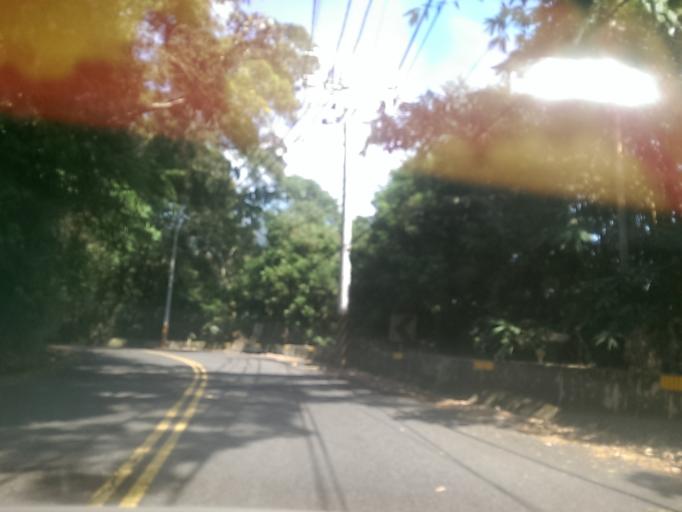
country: TW
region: Taiwan
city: Lugu
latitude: 23.8250
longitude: 120.8226
